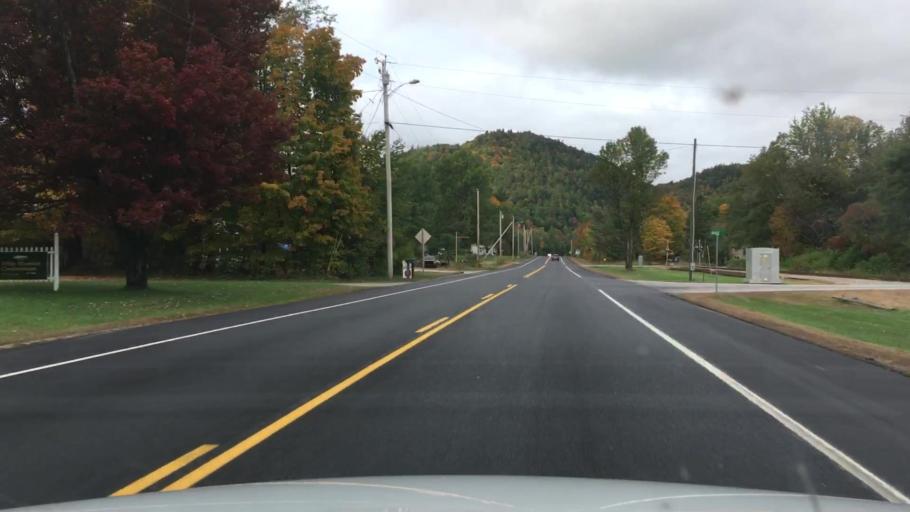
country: US
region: Maine
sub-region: Oxford County
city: Bethel
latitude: 44.3942
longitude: -70.9723
